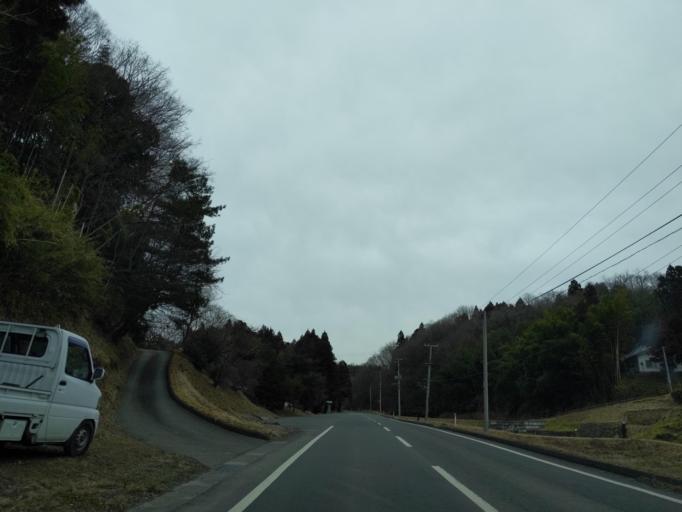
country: JP
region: Fukushima
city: Miharu
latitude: 37.4635
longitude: 140.4476
